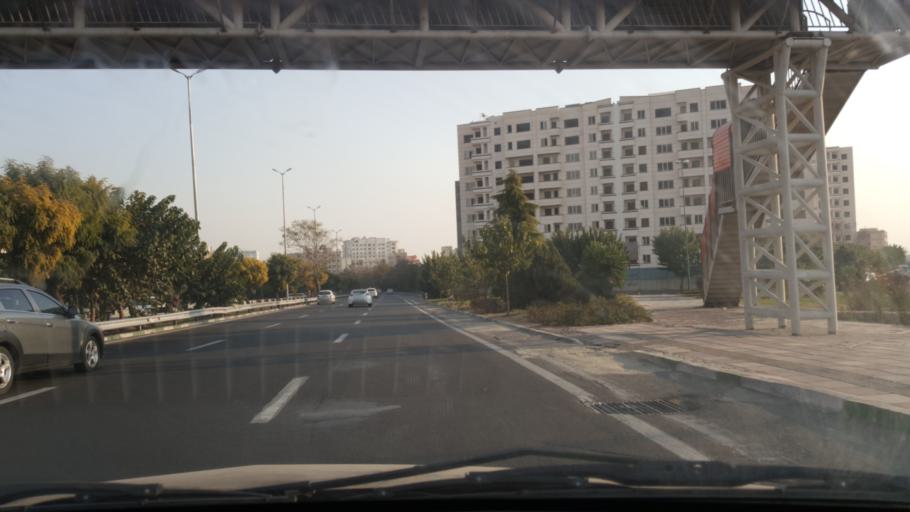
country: IR
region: Tehran
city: Tehran
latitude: 35.7369
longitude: 51.2837
